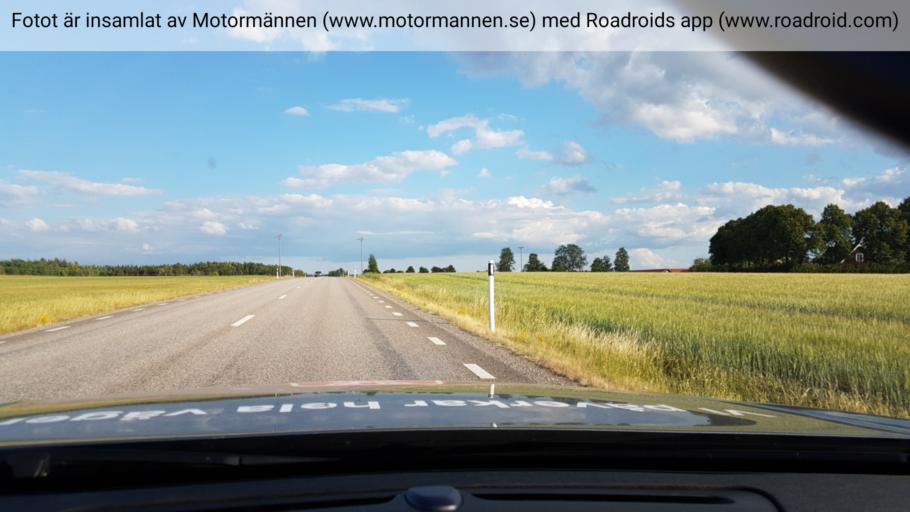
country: SE
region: Uppsala
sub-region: Heby Kommun
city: Heby
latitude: 59.9322
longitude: 16.8716
